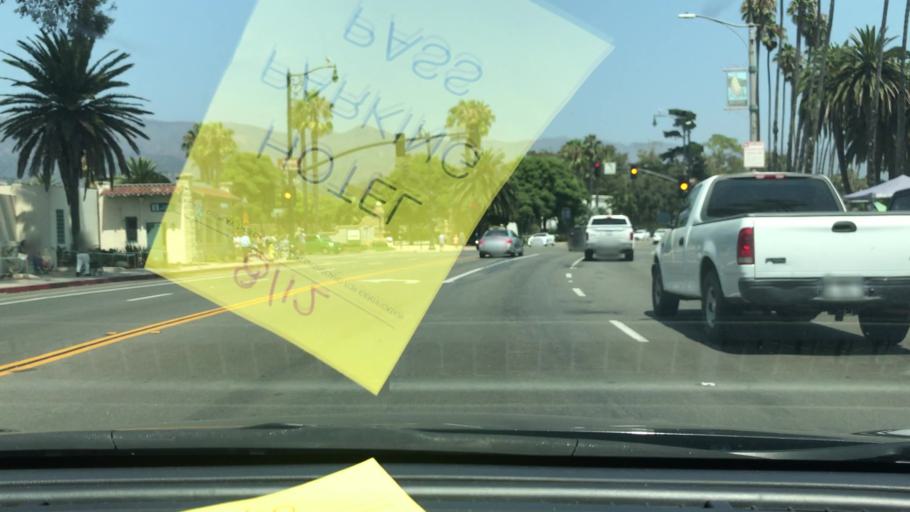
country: US
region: California
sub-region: Santa Barbara County
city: Santa Barbara
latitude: 34.4139
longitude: -119.6873
